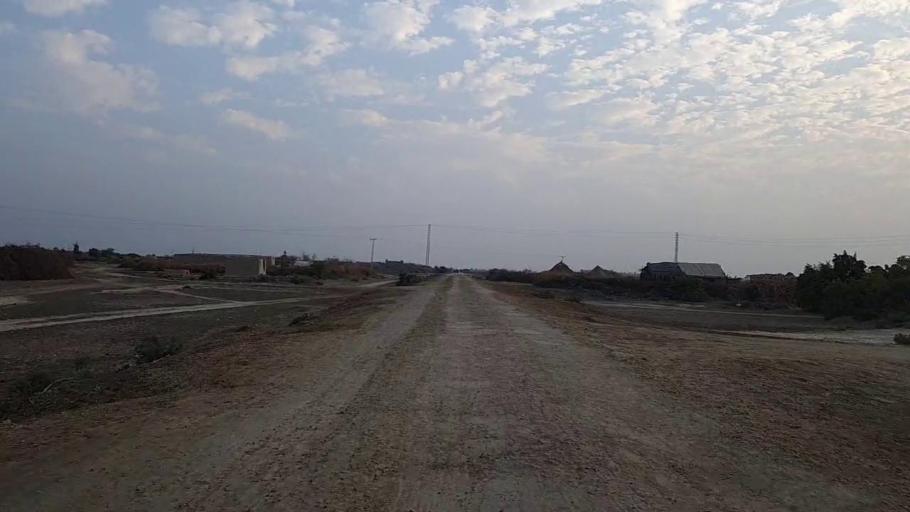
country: PK
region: Sindh
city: Pithoro
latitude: 25.4567
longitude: 69.3454
